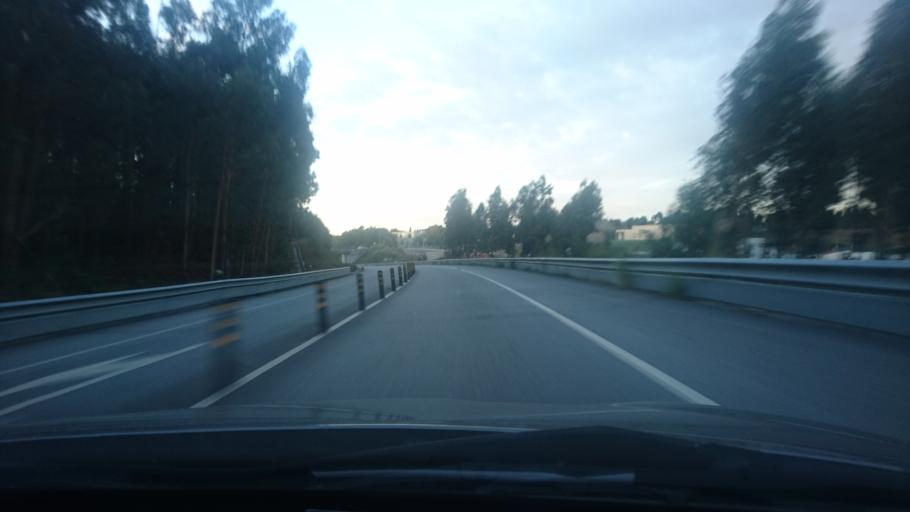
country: PT
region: Aveiro
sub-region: Santa Maria da Feira
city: Arrifana
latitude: 40.9211
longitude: -8.4903
